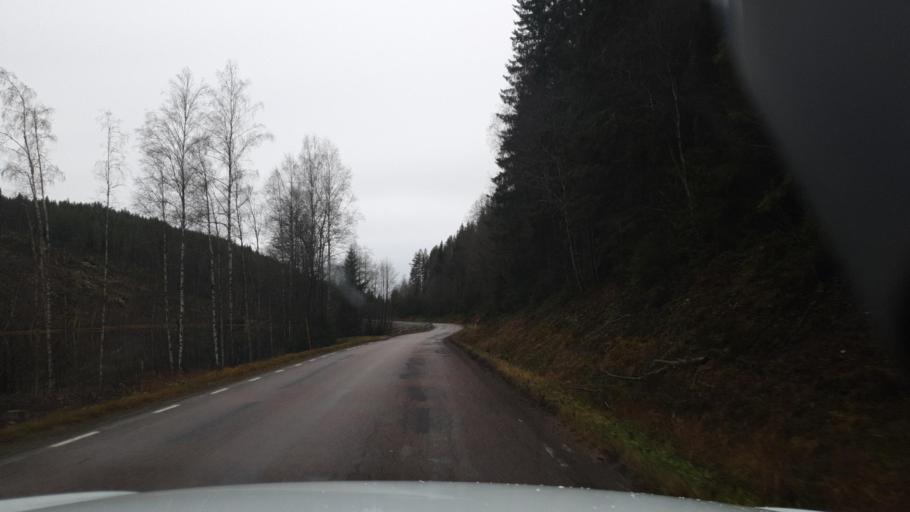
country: SE
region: Vaermland
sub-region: Arvika Kommun
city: Arvika
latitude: 59.7019
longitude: 12.7910
